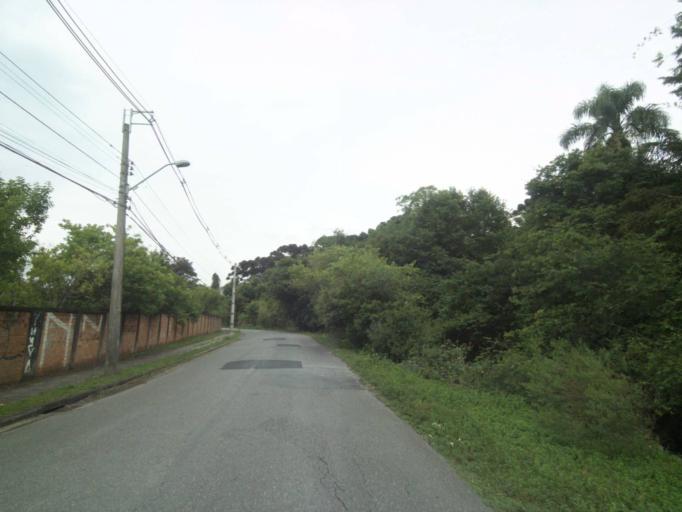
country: BR
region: Parana
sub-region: Curitiba
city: Curitiba
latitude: -25.4119
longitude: -49.3078
